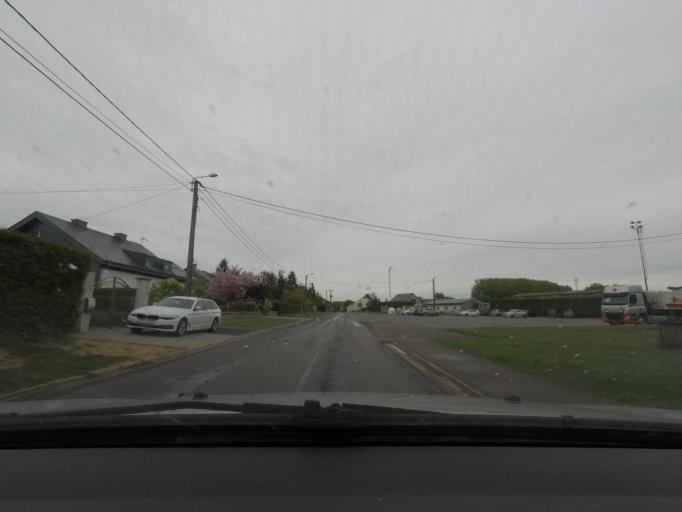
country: BE
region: Wallonia
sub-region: Province du Luxembourg
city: Etalle
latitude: 49.6673
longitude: 5.5616
